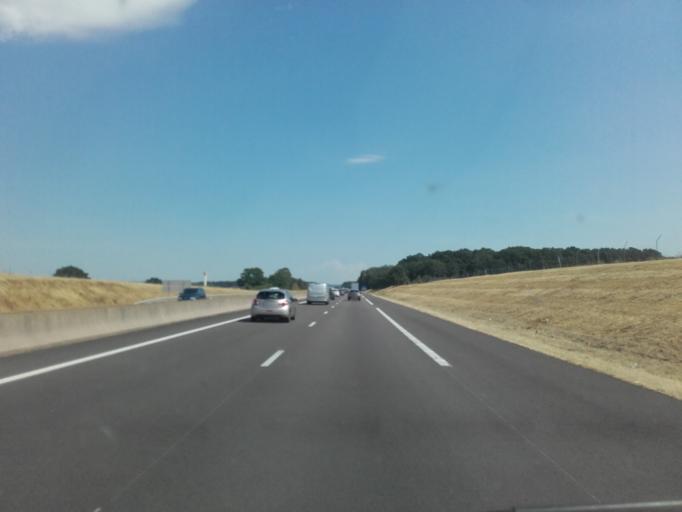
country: FR
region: Bourgogne
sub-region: Departement de la Cote-d'Or
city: Semur-en-Auxois
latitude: 47.3754
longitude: 4.3886
